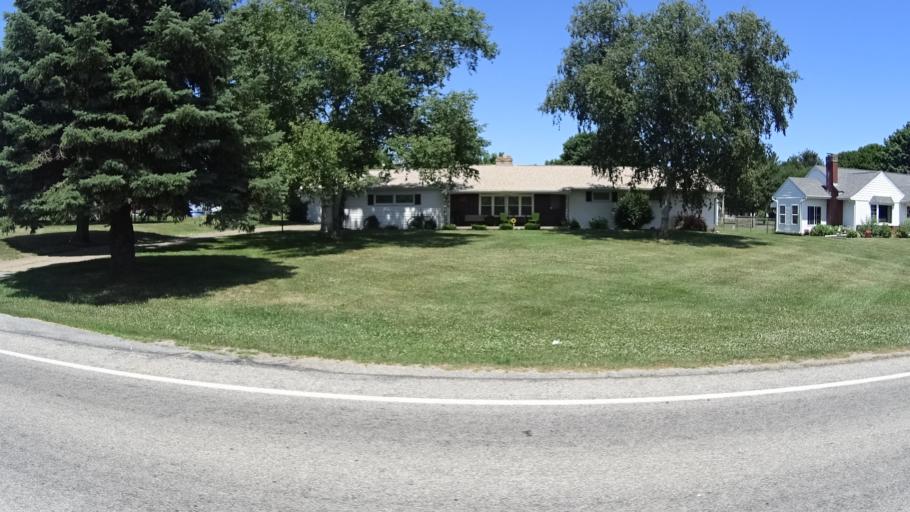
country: US
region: Ohio
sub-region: Erie County
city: Sandusky
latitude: 41.3958
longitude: -82.6585
